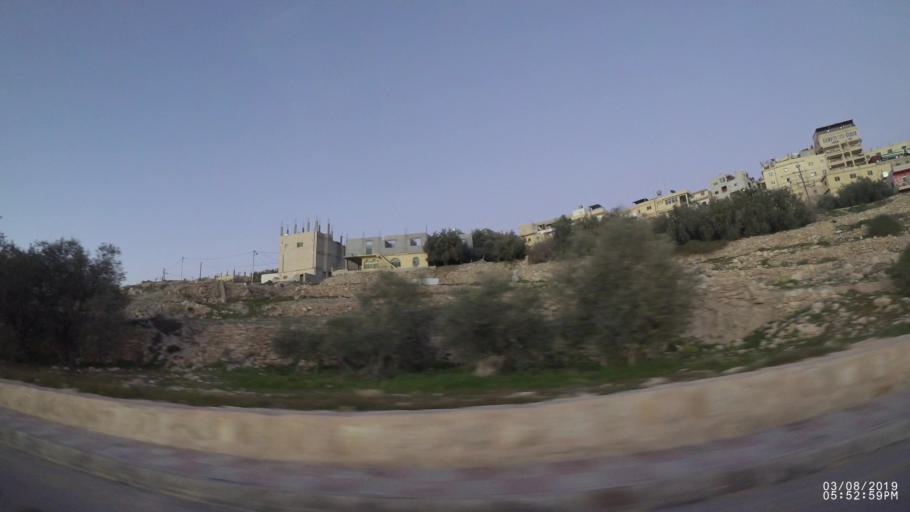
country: JO
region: Ma'an
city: Petra
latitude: 30.3220
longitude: 35.4816
